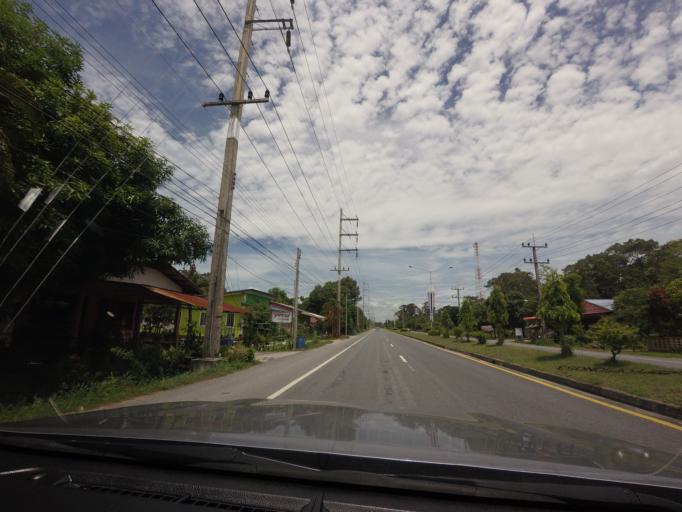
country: TH
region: Songkhla
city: Sathing Phra
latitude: 7.5586
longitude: 100.4138
